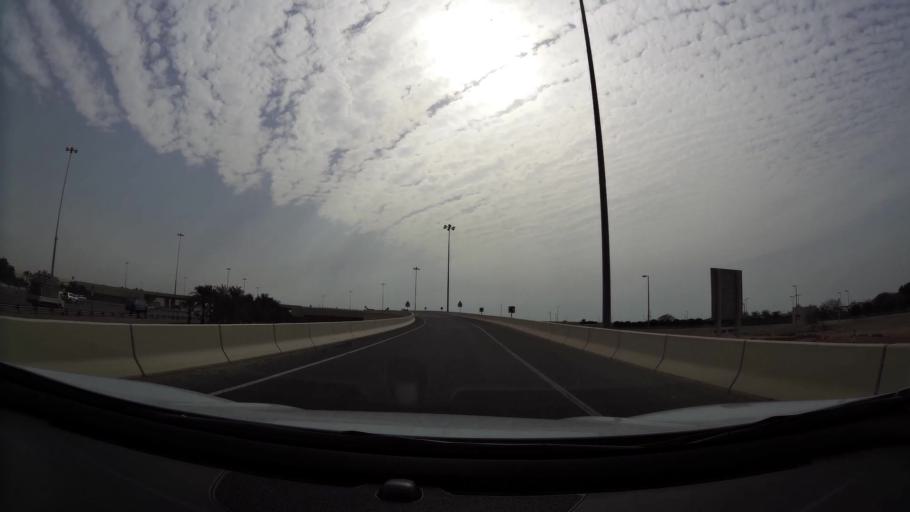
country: AE
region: Abu Dhabi
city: Abu Dhabi
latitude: 24.5133
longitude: 54.6649
